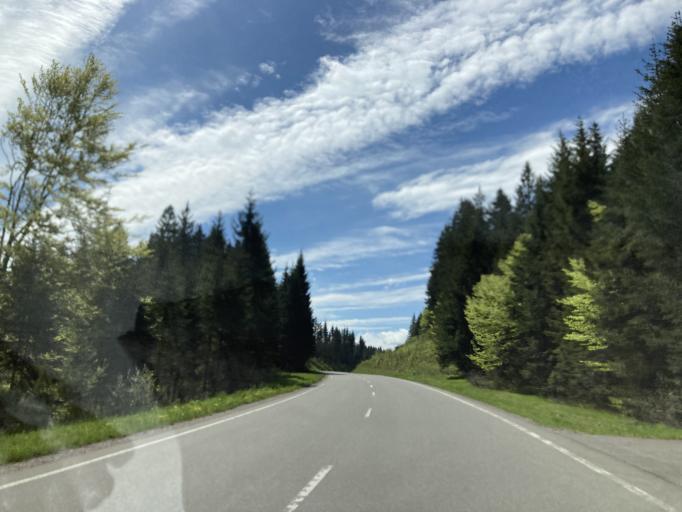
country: DE
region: Baden-Wuerttemberg
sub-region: Freiburg Region
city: Furtwangen im Schwarzwald
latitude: 48.0230
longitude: 8.1961
